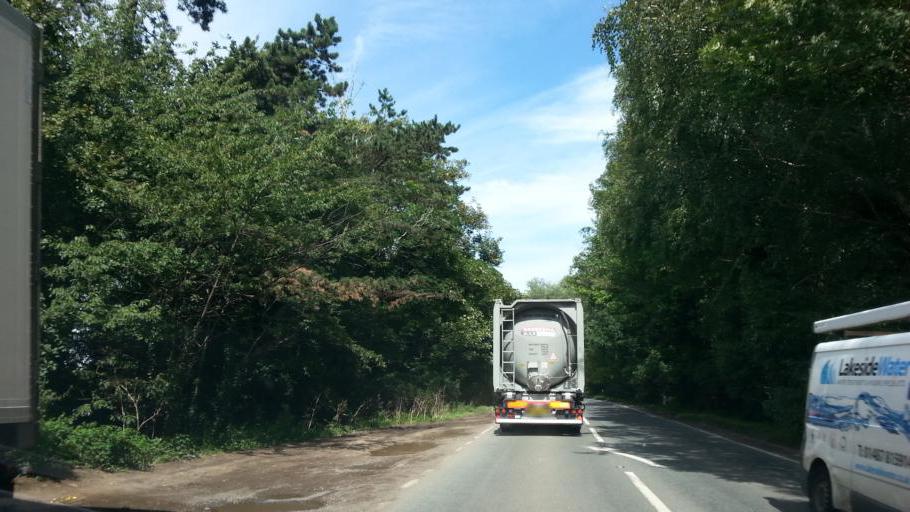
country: GB
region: England
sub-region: Suffolk
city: Exning
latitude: 52.2761
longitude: 0.3940
